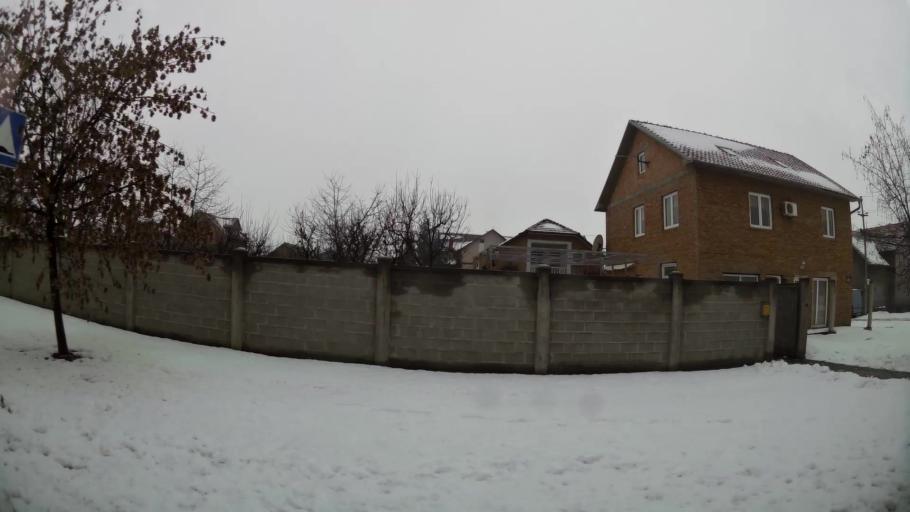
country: RS
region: Central Serbia
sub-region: Belgrade
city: Zemun
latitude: 44.8480
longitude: 20.3438
